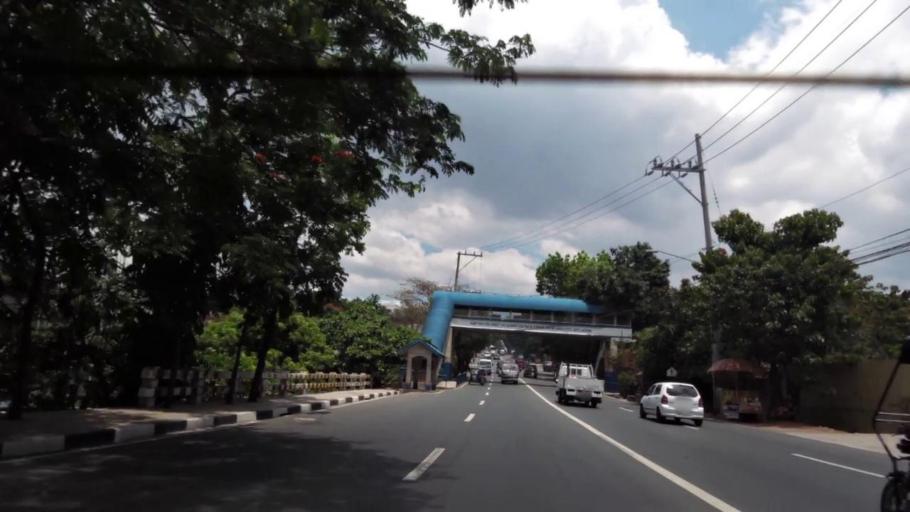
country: PH
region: Calabarzon
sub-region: Province of Rizal
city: Cainta
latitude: 14.5970
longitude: 121.1720
